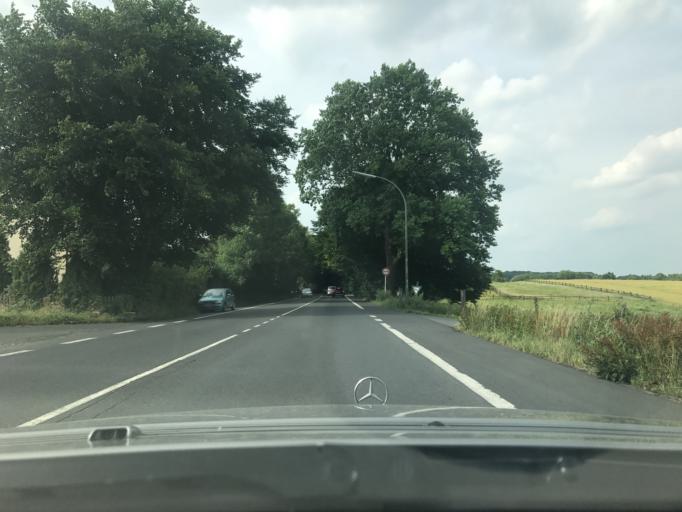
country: DE
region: North Rhine-Westphalia
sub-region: Regierungsbezirk Arnsberg
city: Unna
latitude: 51.4838
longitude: 7.7072
